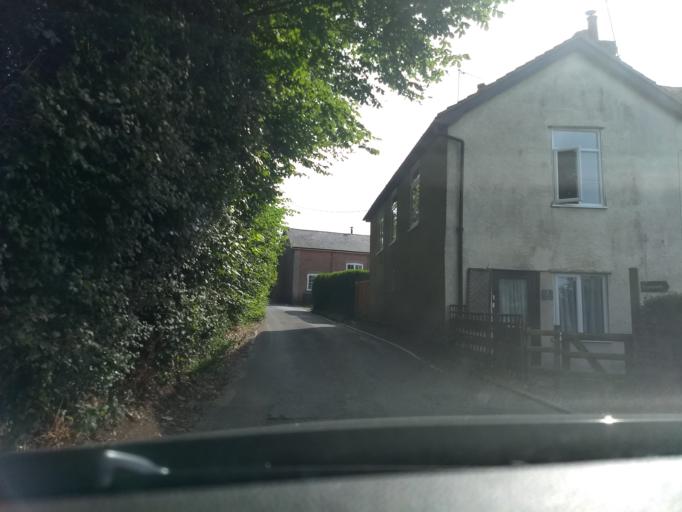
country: GB
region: England
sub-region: Suffolk
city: Shotley Gate
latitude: 51.9903
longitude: 1.2120
